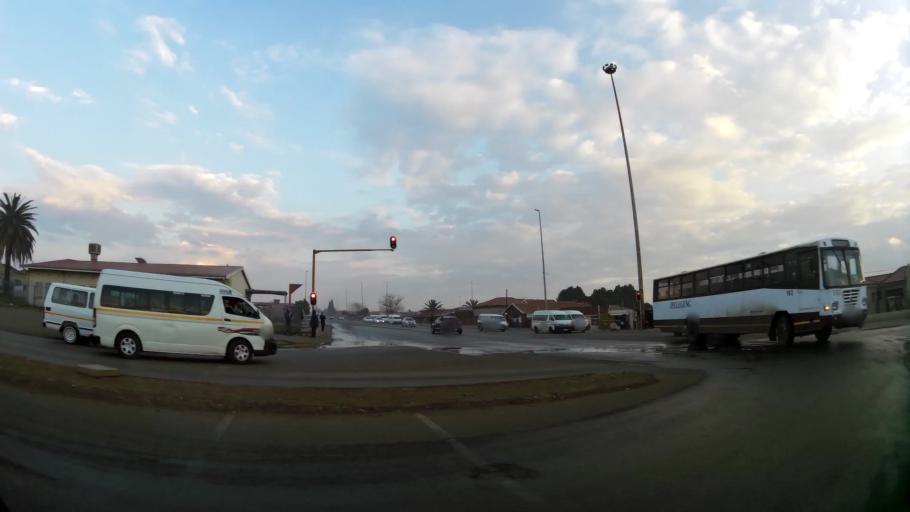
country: ZA
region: Gauteng
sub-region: City of Johannesburg Metropolitan Municipality
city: Orange Farm
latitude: -26.5725
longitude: 27.8385
